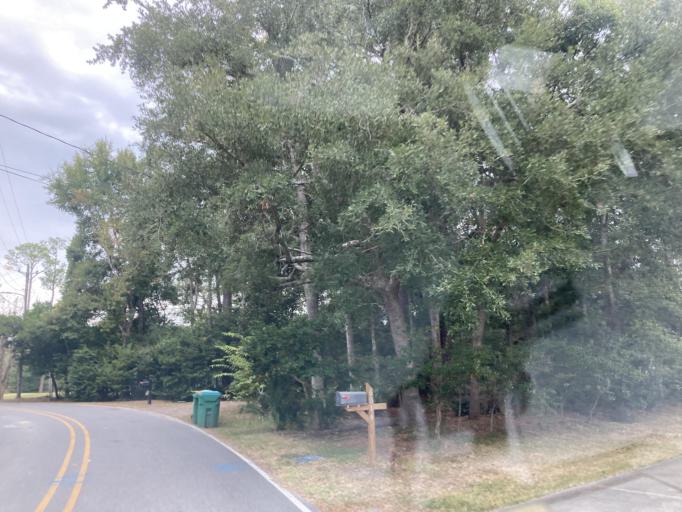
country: US
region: Mississippi
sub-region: Jackson County
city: Gulf Hills
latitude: 30.4294
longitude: -88.8359
